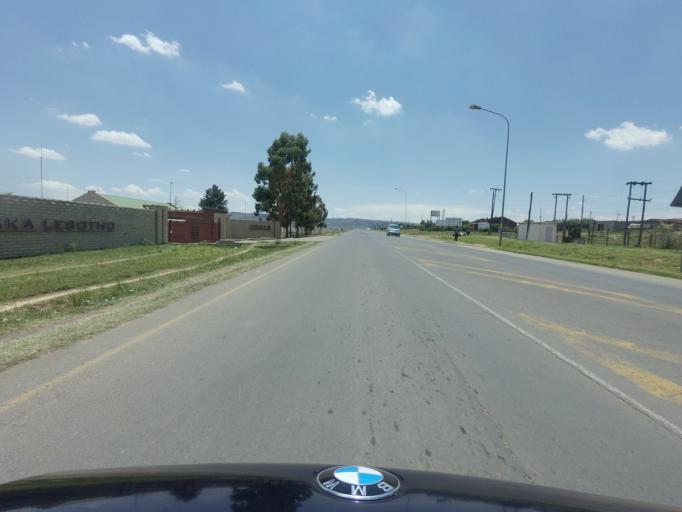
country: LS
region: Maseru
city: Maseru
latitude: -29.2684
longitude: 27.5382
